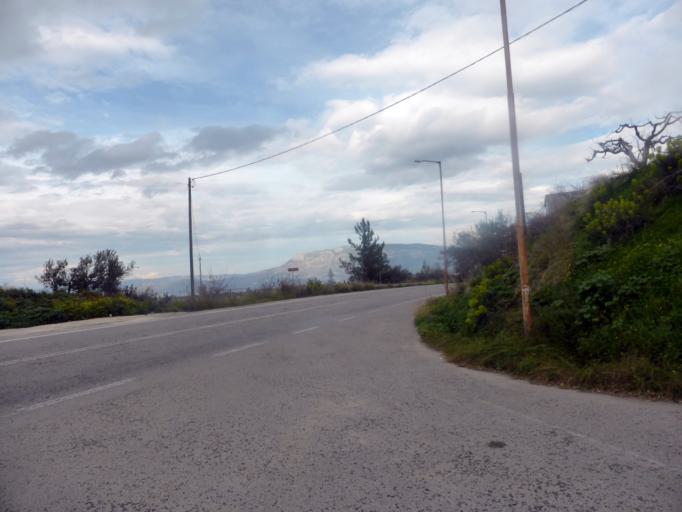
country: GR
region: Peloponnese
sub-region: Nomos Korinthias
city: Arkhaia Korinthos
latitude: 37.9138
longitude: 22.8877
